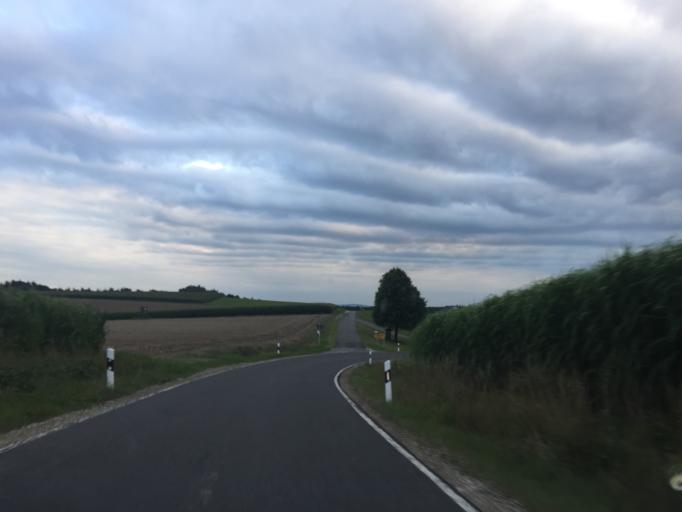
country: DE
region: Bavaria
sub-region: Upper Palatinate
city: Schwarzenbach
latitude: 49.7779
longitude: 12.0316
